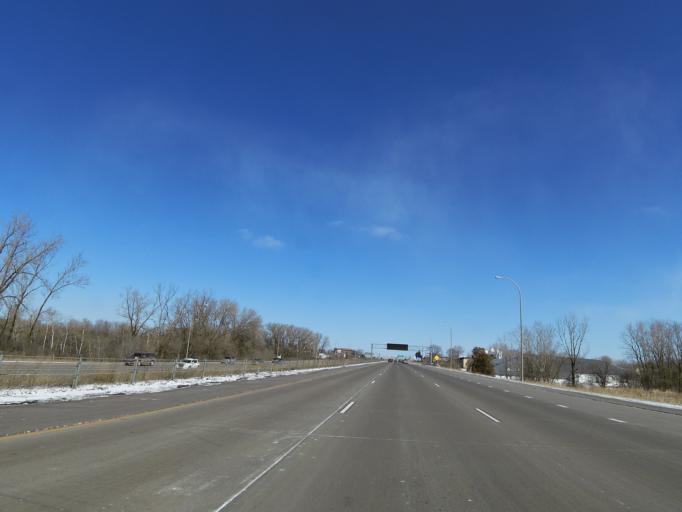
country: US
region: Minnesota
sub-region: Washington County
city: Woodbury
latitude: 44.9168
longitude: -92.9783
